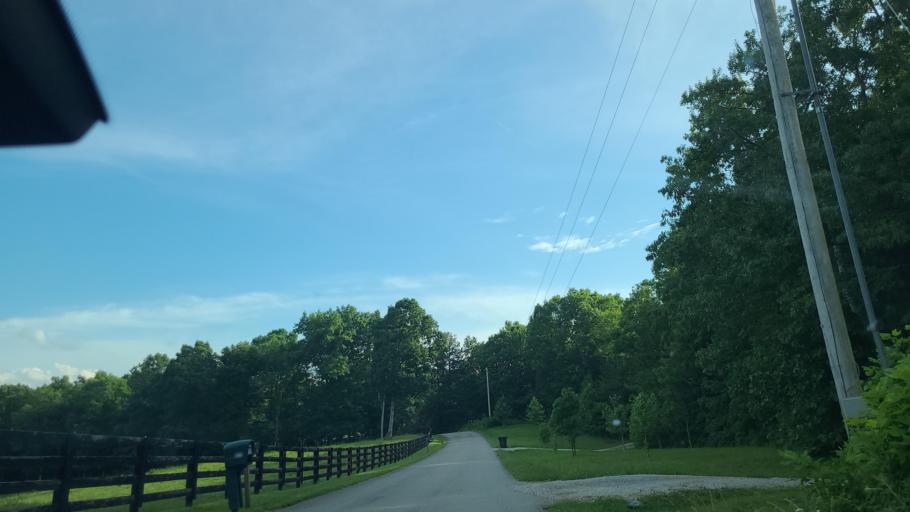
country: US
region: Kentucky
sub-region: Whitley County
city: Corbin
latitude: 36.8857
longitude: -84.2358
